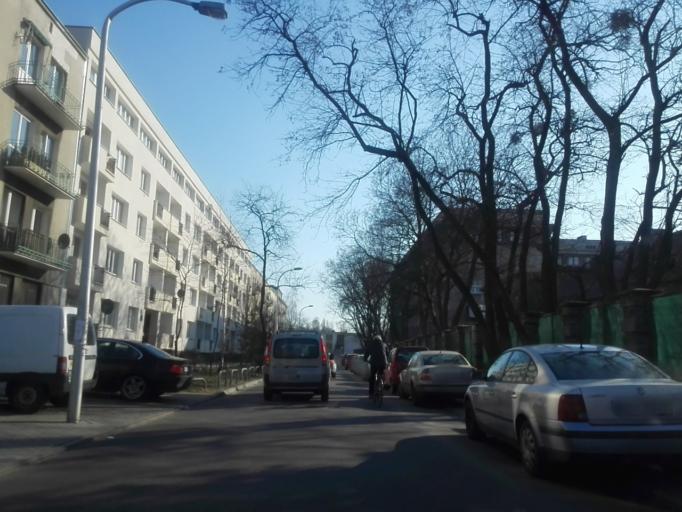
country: PL
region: Masovian Voivodeship
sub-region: Warszawa
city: Mokotow
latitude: 52.2038
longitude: 21.0427
